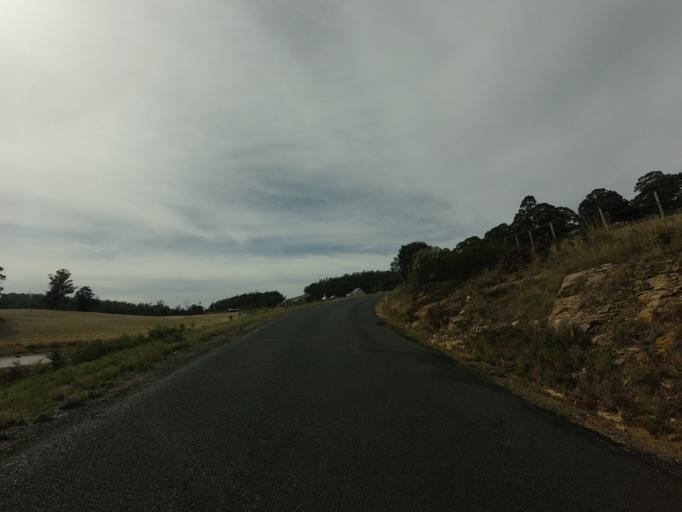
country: AU
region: Tasmania
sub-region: Sorell
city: Sorell
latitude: -42.4443
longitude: 147.5446
